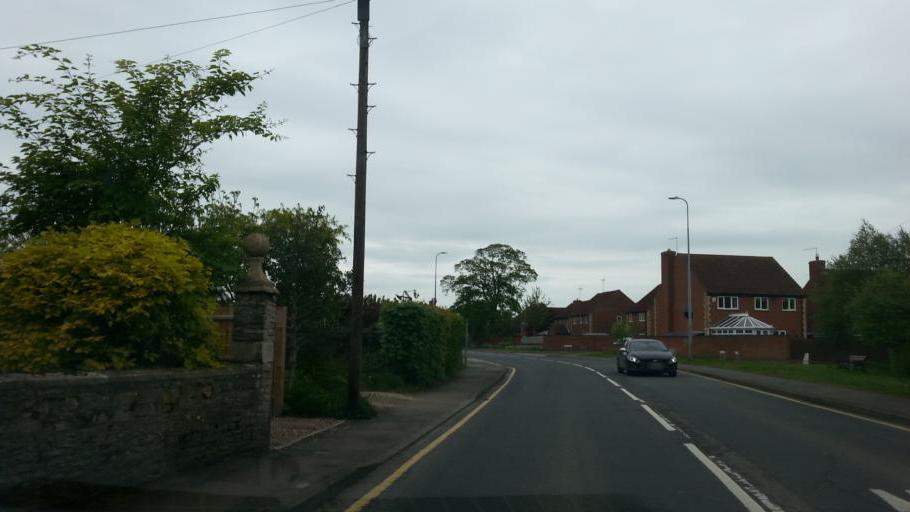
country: GB
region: England
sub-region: Lincolnshire
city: Market Deeping
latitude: 52.6792
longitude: -0.3208
